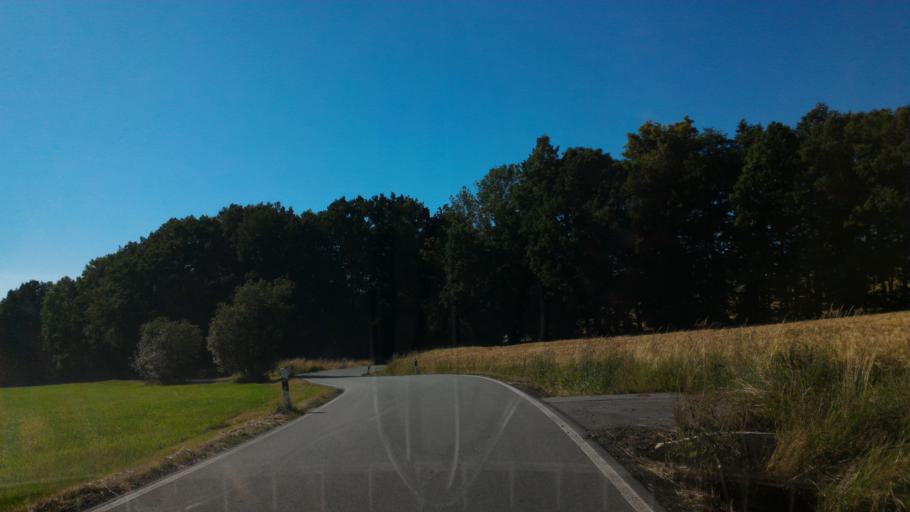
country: DE
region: Saxony
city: Mittelherwigsdorf
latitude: 50.9366
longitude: 14.7582
